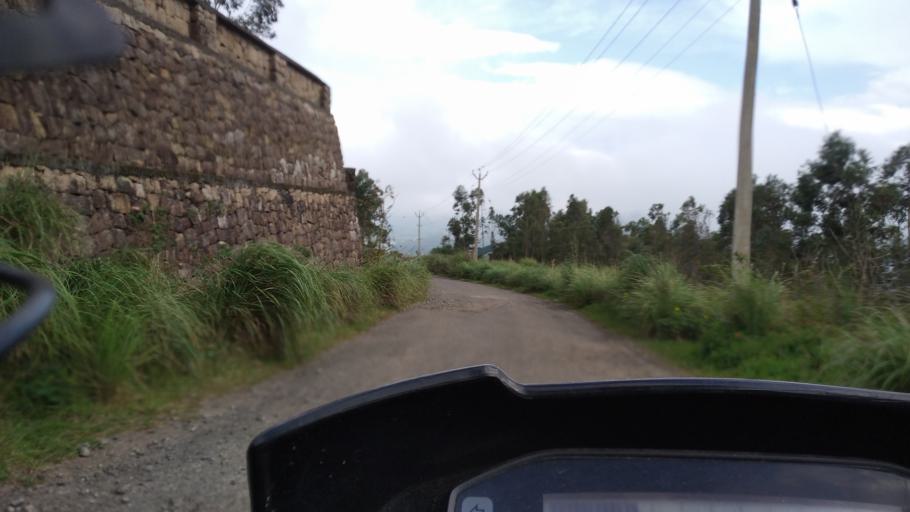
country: IN
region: Kerala
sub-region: Idukki
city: Munnar
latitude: 10.0395
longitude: 77.1806
